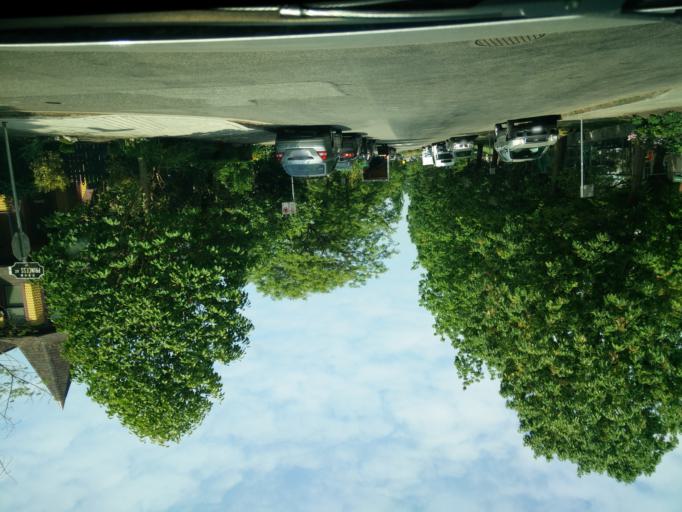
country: CA
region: British Columbia
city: Vancouver
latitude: 49.2793
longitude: -123.0917
